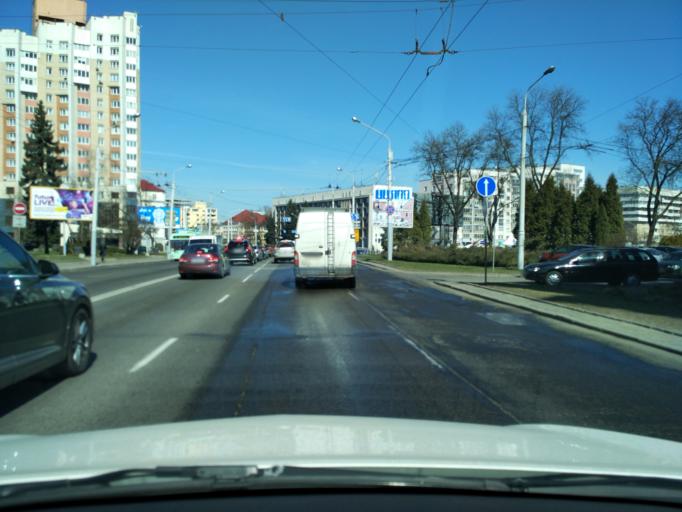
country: BY
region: Minsk
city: Minsk
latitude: 53.8778
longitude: 27.5334
